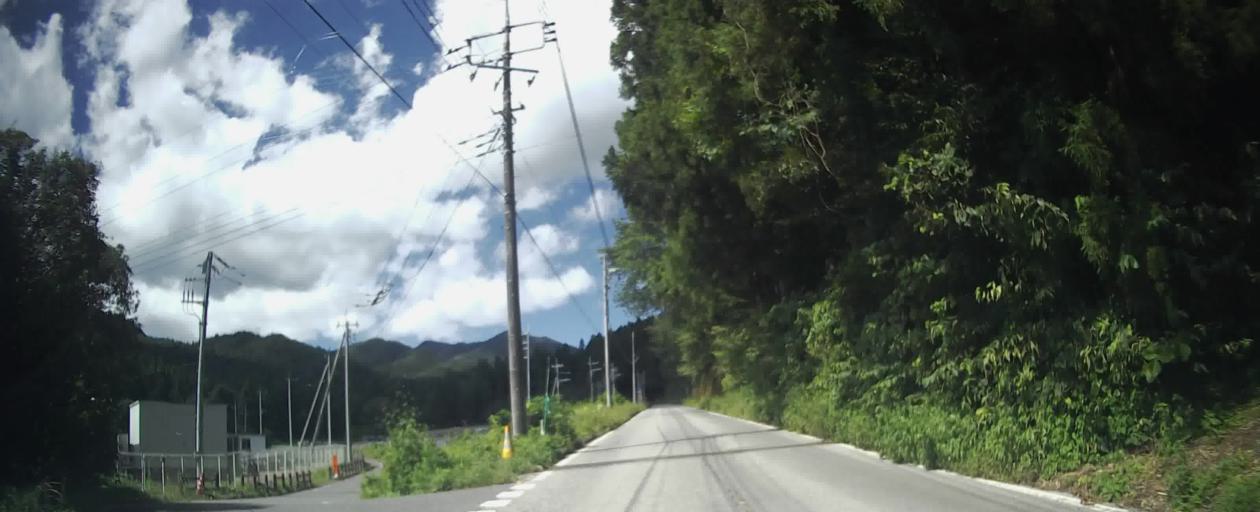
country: JP
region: Gunma
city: Kanekomachi
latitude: 36.4377
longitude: 138.9160
